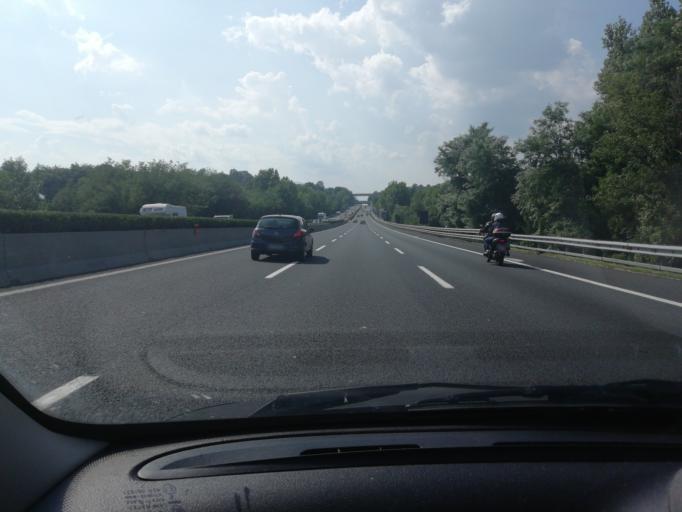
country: IT
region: Latium
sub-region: Provincia di Frosinone
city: Arnara
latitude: 41.5663
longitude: 13.3929
